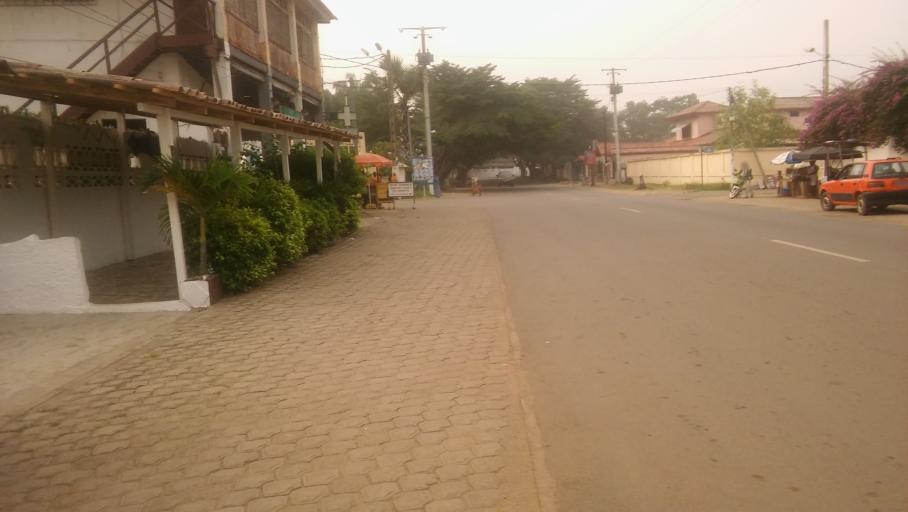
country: CI
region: Sud-Comoe
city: Grand-Bassam
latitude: 5.1975
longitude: -3.7374
